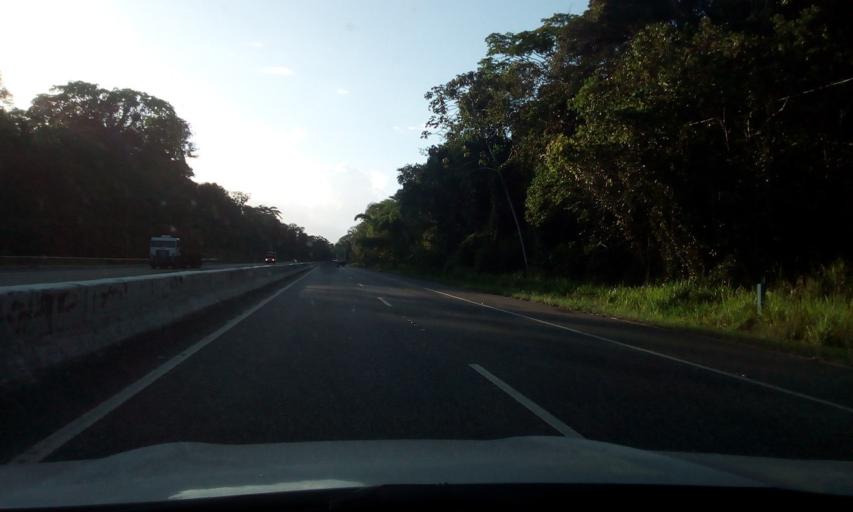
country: BR
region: Pernambuco
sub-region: Goiana
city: Goiana
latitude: -7.5981
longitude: -34.9824
